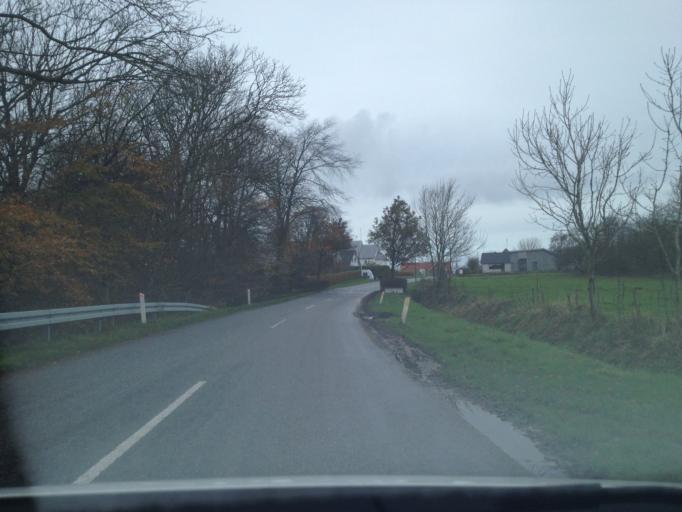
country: DK
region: South Denmark
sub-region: Tonder Kommune
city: Sherrebek
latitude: 55.2430
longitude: 8.8296
